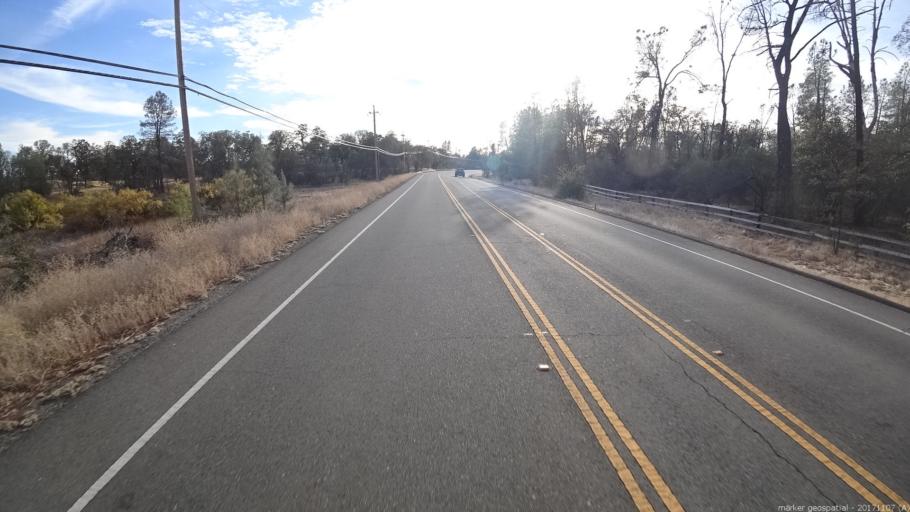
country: US
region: California
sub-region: Shasta County
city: Shasta
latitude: 40.5205
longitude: -122.4790
